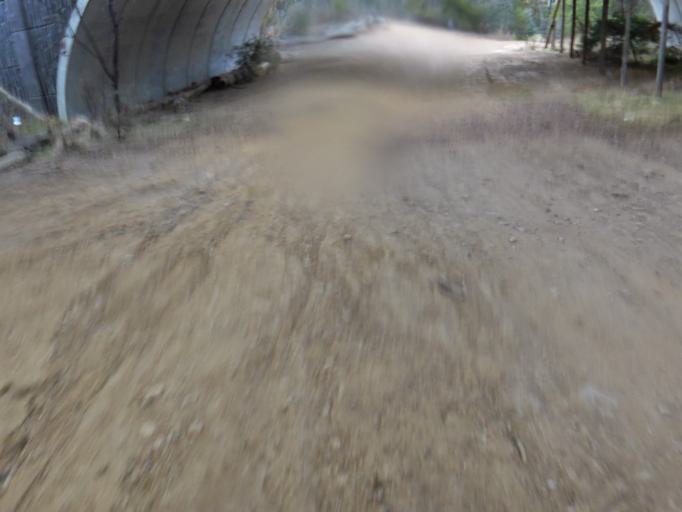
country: AU
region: Australian Capital Territory
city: Macquarie
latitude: -35.2685
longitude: 149.0874
